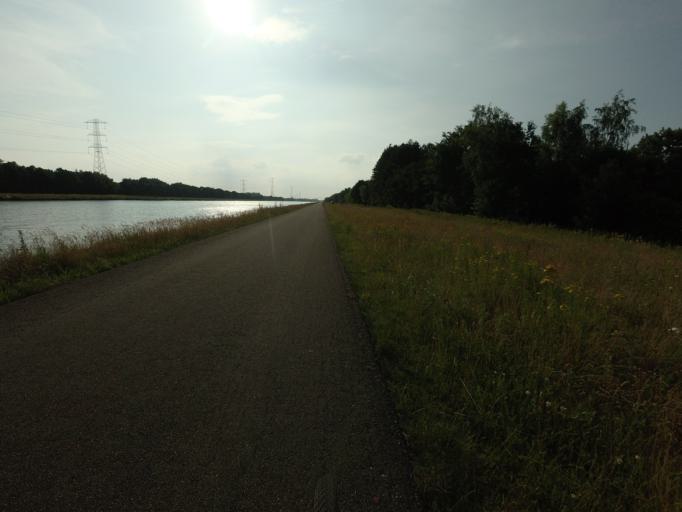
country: BE
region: Flanders
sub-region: Provincie Antwerpen
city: Nijlen
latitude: 51.1879
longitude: 4.6841
